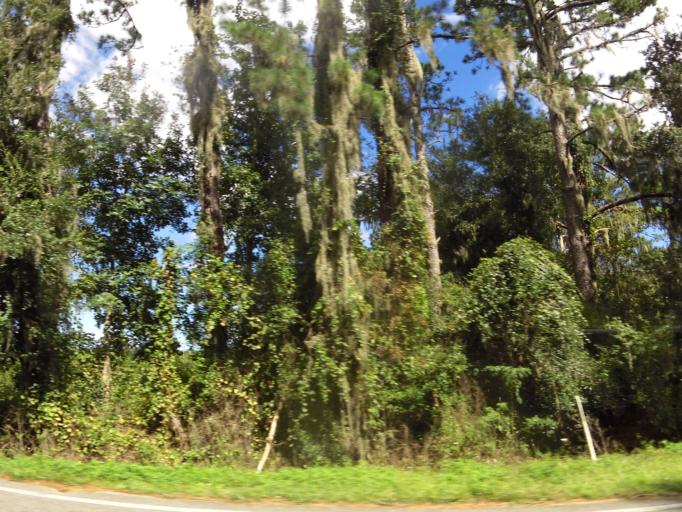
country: US
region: Florida
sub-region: Saint Johns County
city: Saint Augustine South
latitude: 29.8130
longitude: -81.4845
